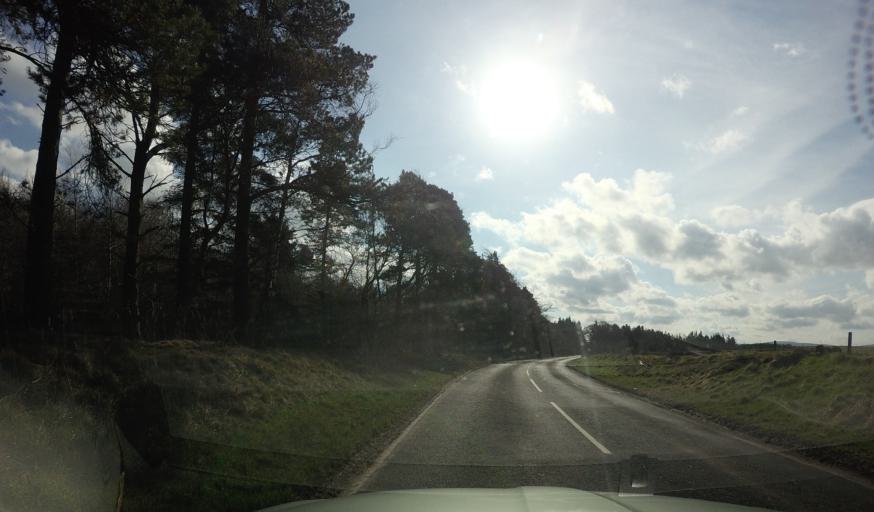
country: GB
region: Scotland
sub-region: Midlothian
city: Penicuik
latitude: 55.8164
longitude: -3.1992
